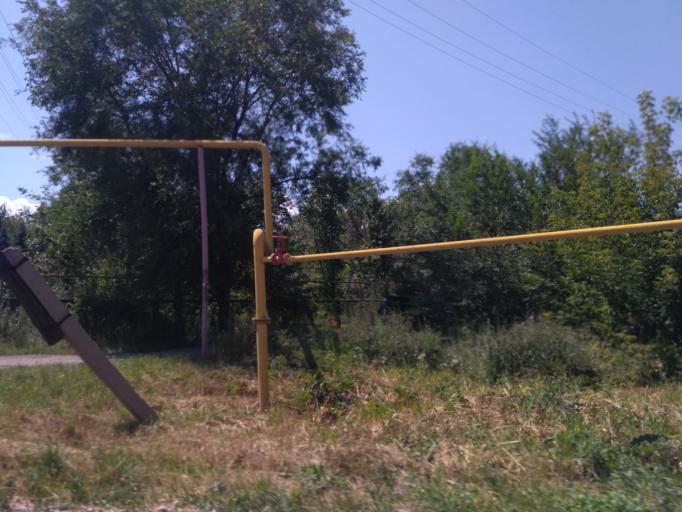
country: KZ
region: Almaty Oblysy
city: Burunday
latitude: 43.1657
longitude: 76.6070
